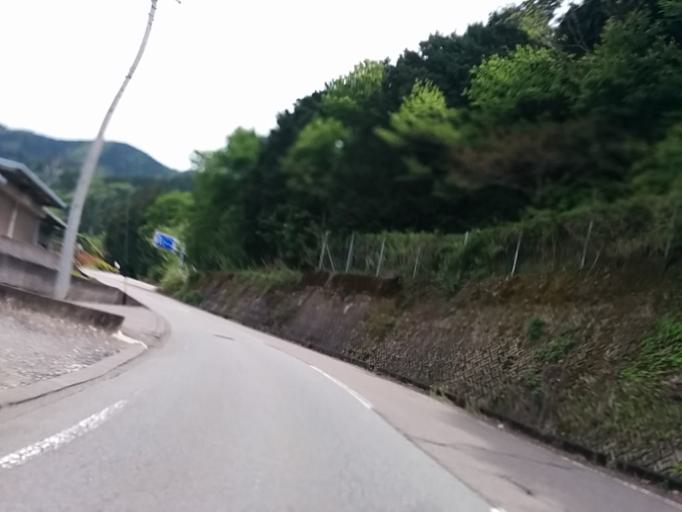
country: JP
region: Gifu
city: Gujo
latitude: 35.7292
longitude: 136.9549
